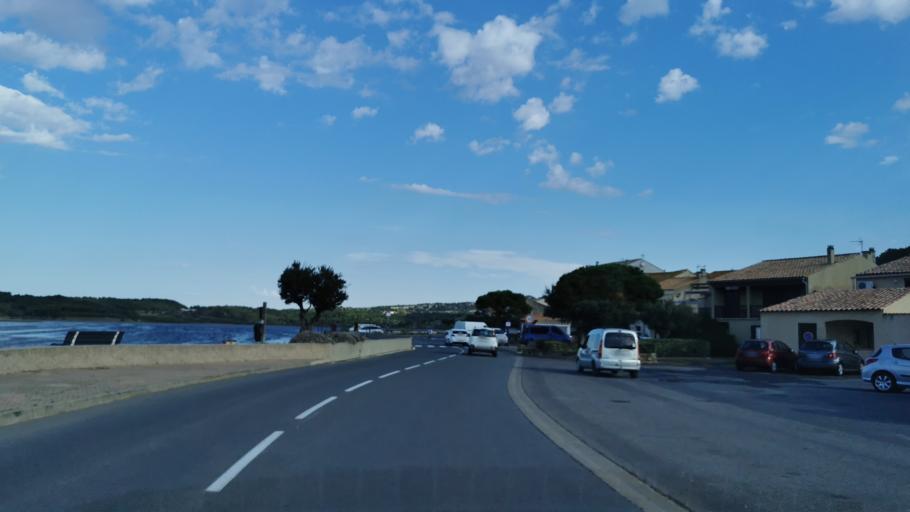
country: FR
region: Languedoc-Roussillon
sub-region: Departement de l'Aude
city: Gruissan
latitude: 43.1058
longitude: 3.0838
